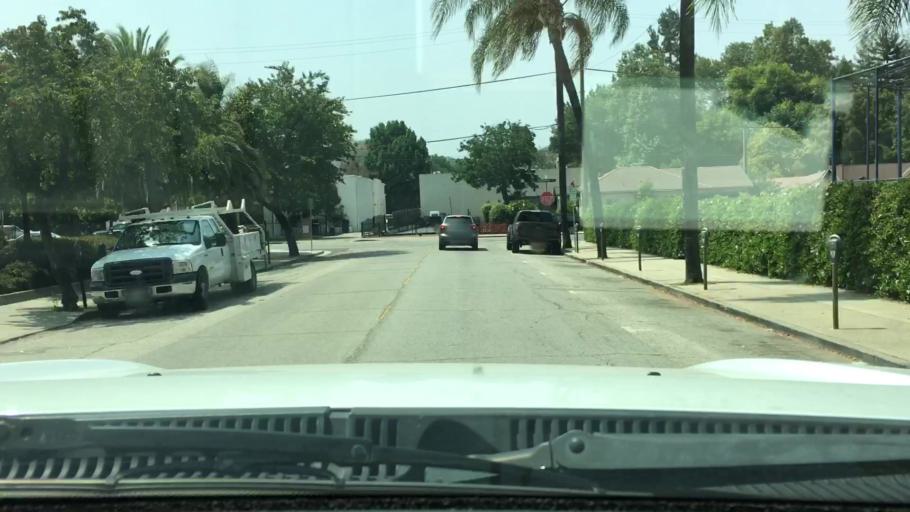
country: US
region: California
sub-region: San Luis Obispo County
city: San Luis Obispo
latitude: 35.2800
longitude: -120.6666
